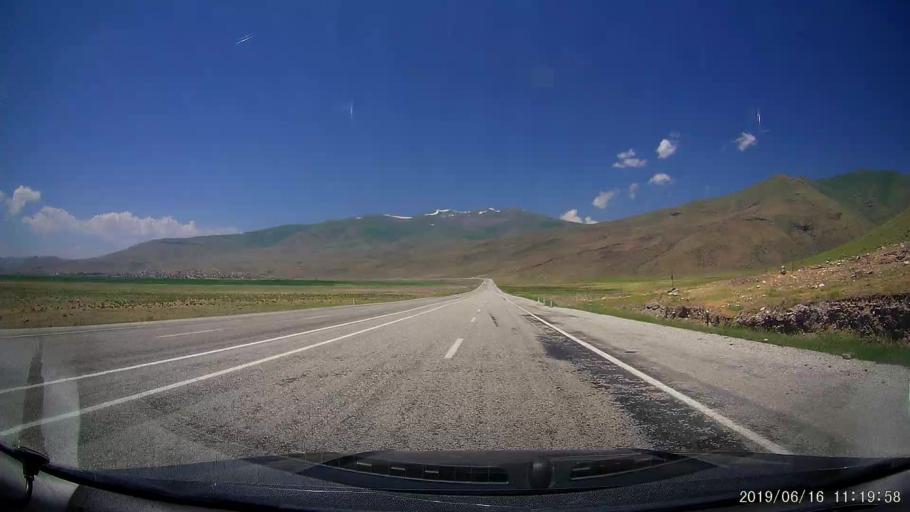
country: TR
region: Agri
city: Dogubayazit
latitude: 39.6962
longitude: 44.1022
